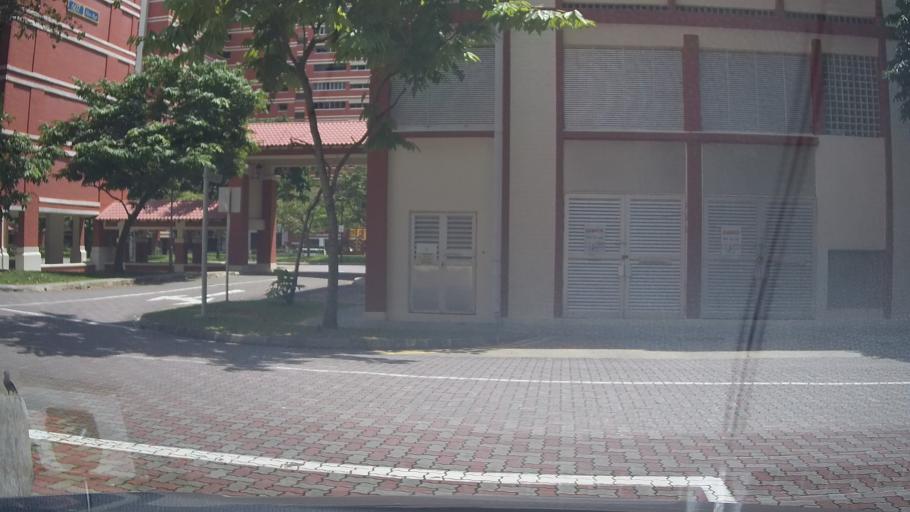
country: MY
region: Johor
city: Kampung Pasir Gudang Baru
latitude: 1.3762
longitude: 103.9420
